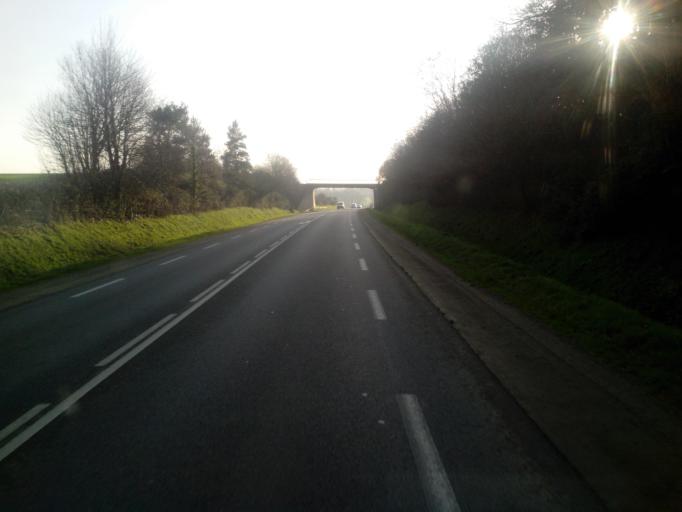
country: FR
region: Brittany
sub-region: Departement du Morbihan
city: Loyat
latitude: 47.9684
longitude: -2.3831
